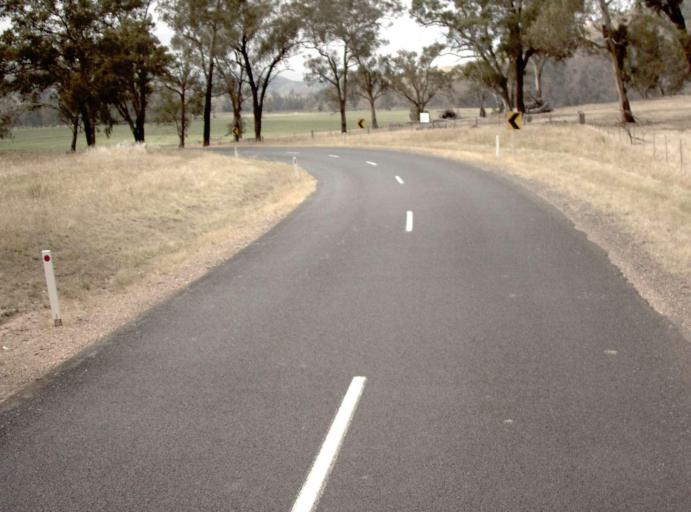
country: AU
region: Victoria
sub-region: Wellington
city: Heyfield
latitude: -37.6334
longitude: 146.6238
